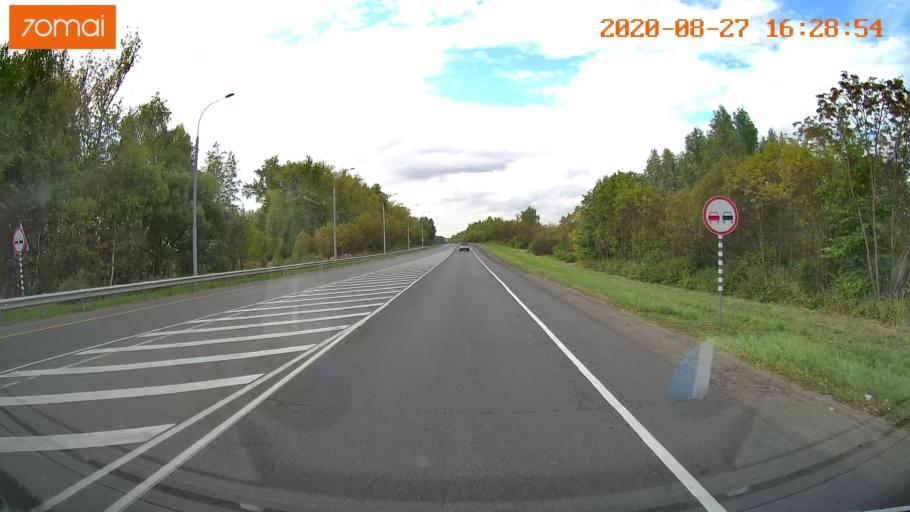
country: RU
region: Vladimir
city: Bogolyubovo
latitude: 56.2014
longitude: 40.4453
